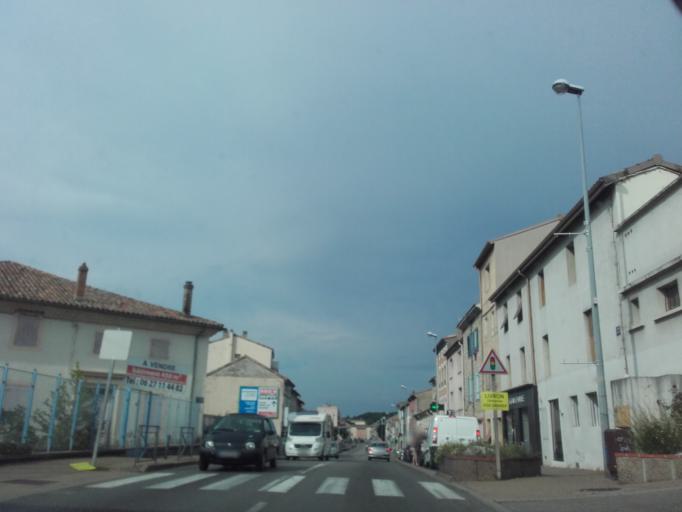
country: FR
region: Rhone-Alpes
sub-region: Departement de la Drome
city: Livron-sur-Drome
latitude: 44.7720
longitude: 4.8430
